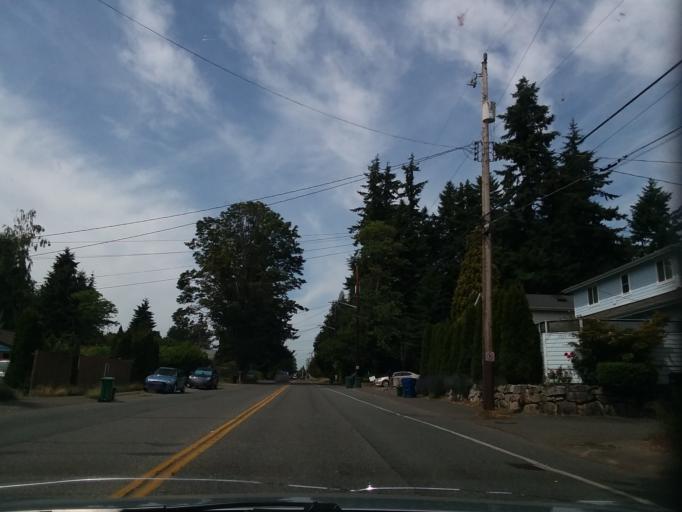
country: US
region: Washington
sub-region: King County
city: Shoreline
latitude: 47.7091
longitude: -122.3124
